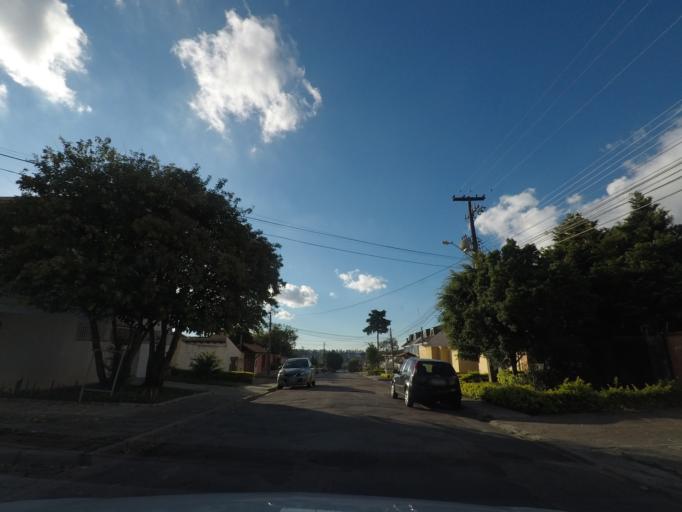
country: BR
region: Parana
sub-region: Sao Jose Dos Pinhais
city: Sao Jose dos Pinhais
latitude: -25.4998
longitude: -49.2523
